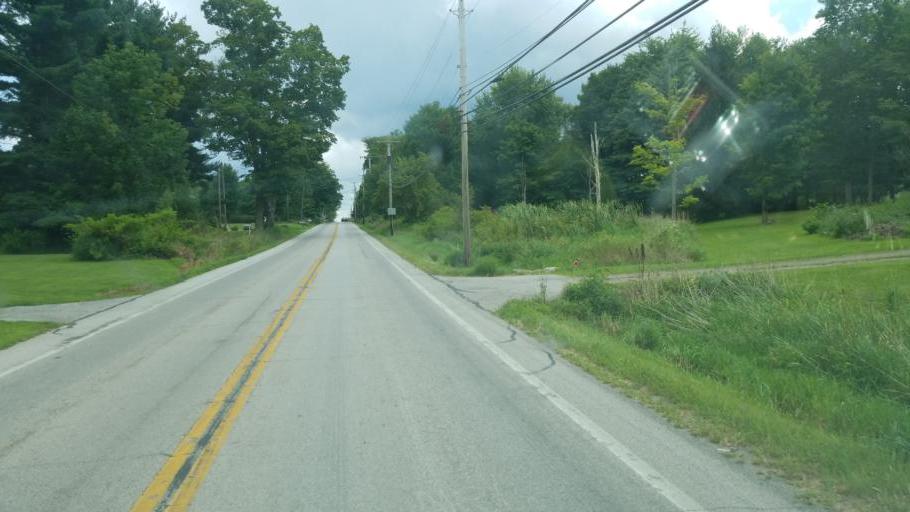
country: US
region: Ohio
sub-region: Ashtabula County
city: Andover
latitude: 41.6070
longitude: -80.6118
